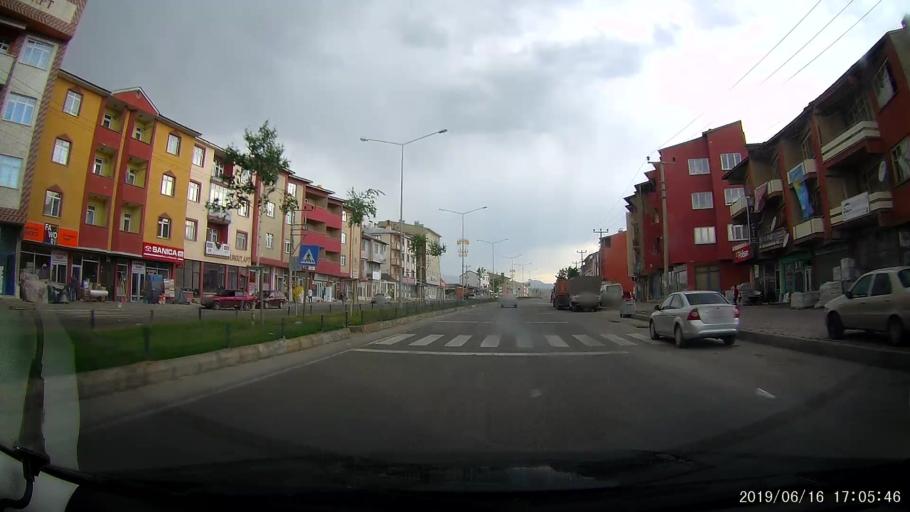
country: TR
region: Erzurum
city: Askale
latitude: 39.9204
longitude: 40.6962
